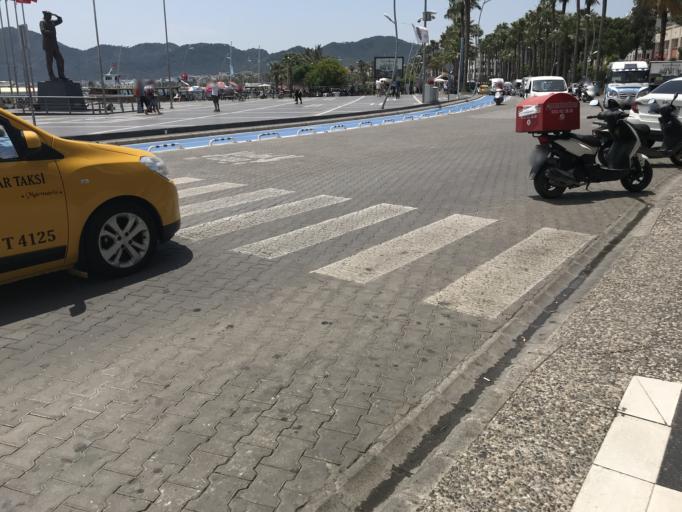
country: TR
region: Mugla
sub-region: Marmaris
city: Marmaris
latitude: 36.8532
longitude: 28.2714
